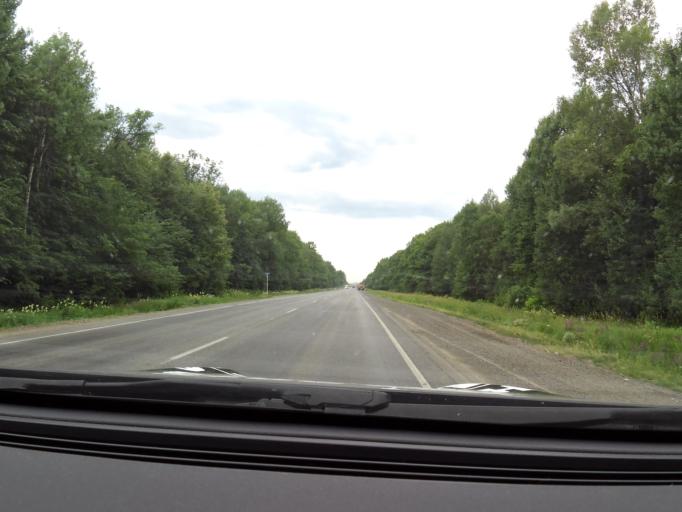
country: RU
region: Bashkortostan
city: Urman
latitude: 54.8175
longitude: 56.8485
